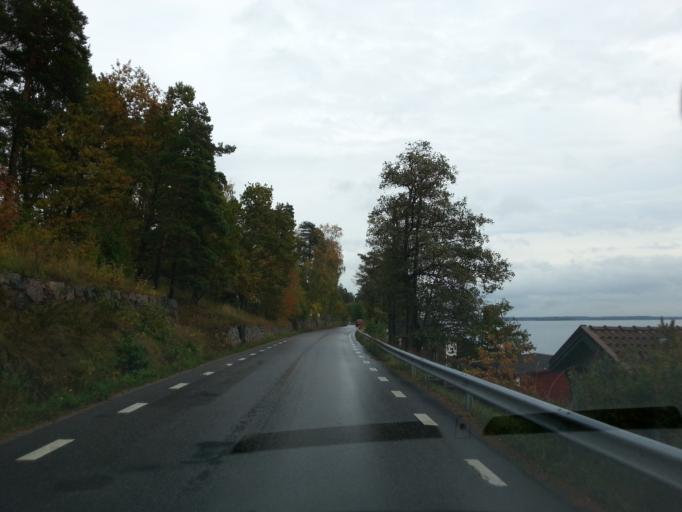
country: SE
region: OEstergoetland
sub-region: Norrkopings Kommun
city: Krokek
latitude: 58.6646
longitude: 16.3605
